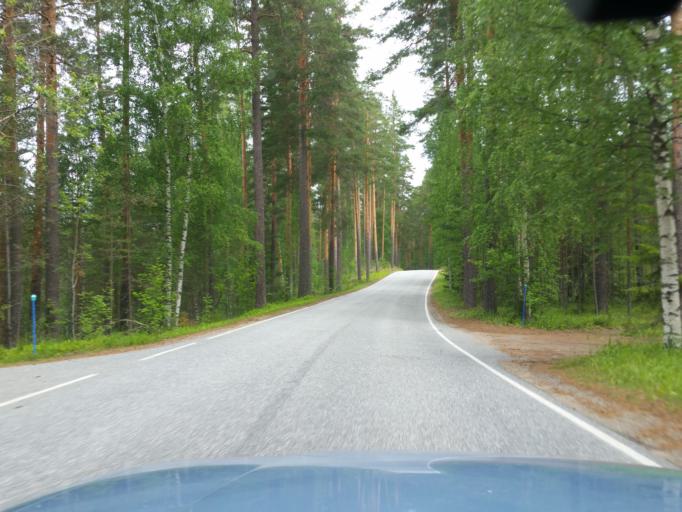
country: FI
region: Southern Savonia
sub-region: Savonlinna
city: Sulkava
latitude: 61.7870
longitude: 28.4252
